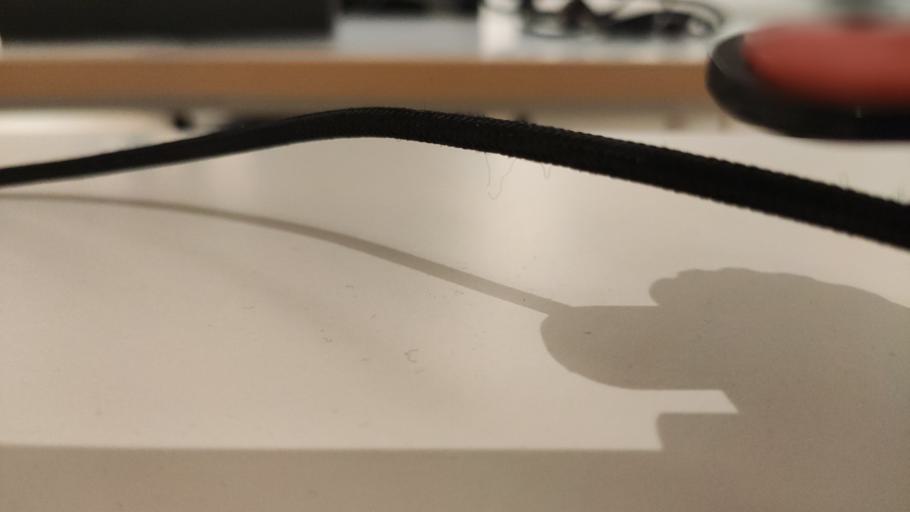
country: RU
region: Moskovskaya
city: Dorokhovo
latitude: 55.4774
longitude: 36.3572
